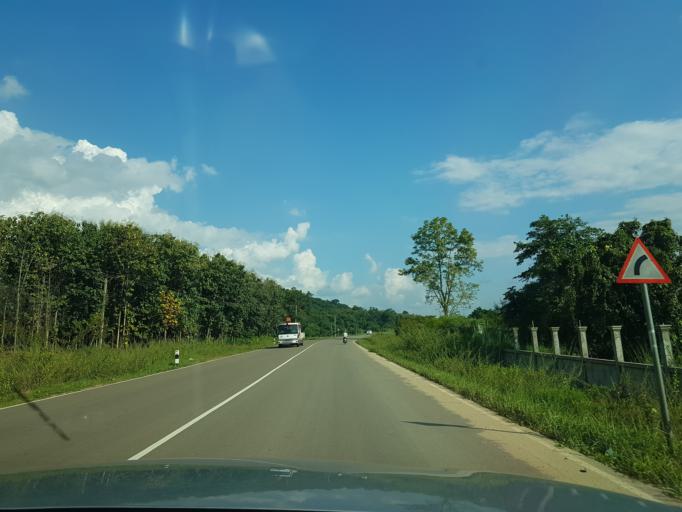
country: TH
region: Nong Khai
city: Pho Tak
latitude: 18.0025
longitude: 102.4093
